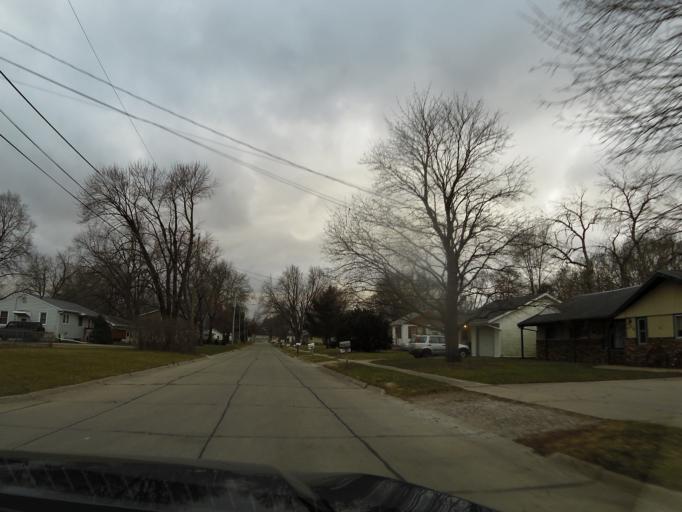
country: US
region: Iowa
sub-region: Black Hawk County
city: Evansdale
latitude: 42.4664
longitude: -92.2953
